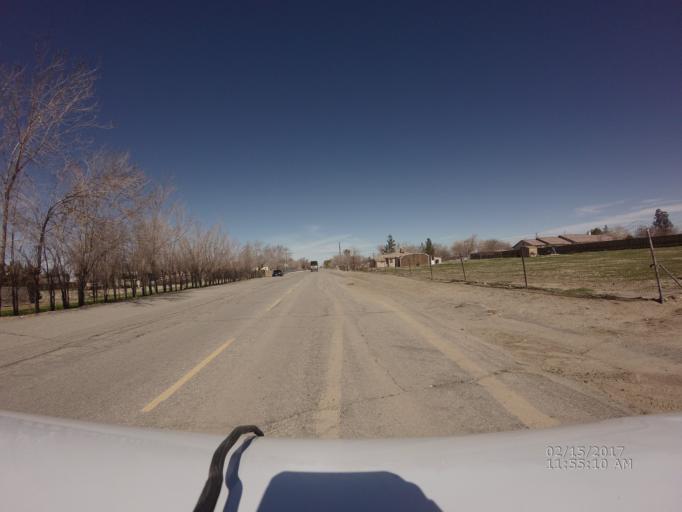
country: US
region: California
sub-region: Los Angeles County
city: Littlerock
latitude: 34.5733
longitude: -117.9610
